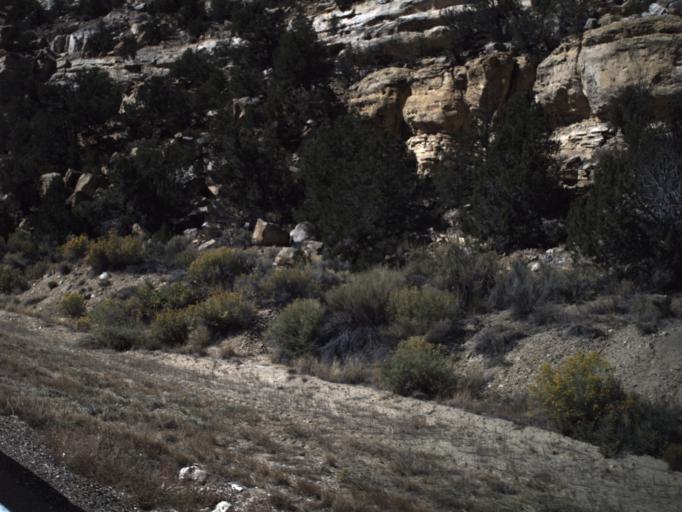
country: US
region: Utah
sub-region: Wayne County
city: Loa
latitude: 37.7382
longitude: -111.7421
